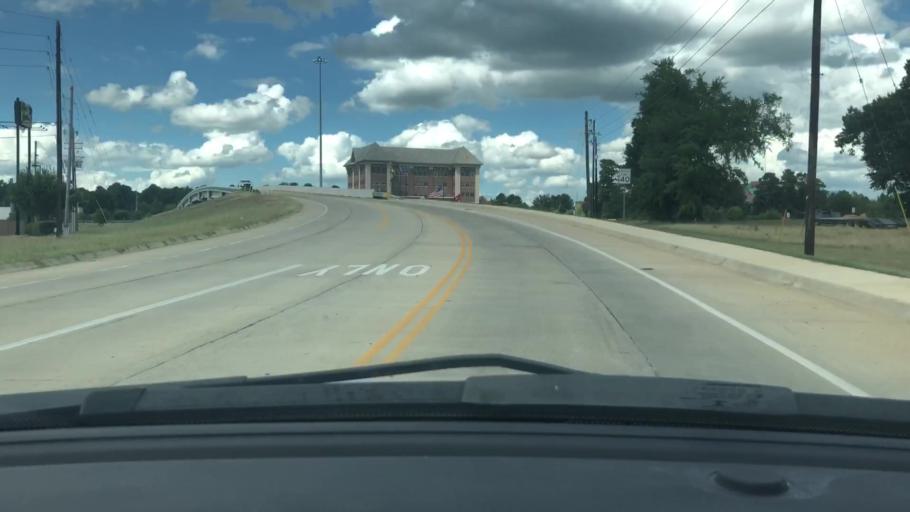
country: US
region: Arkansas
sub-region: Miller County
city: Texarkana
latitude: 33.4588
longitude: -94.0763
